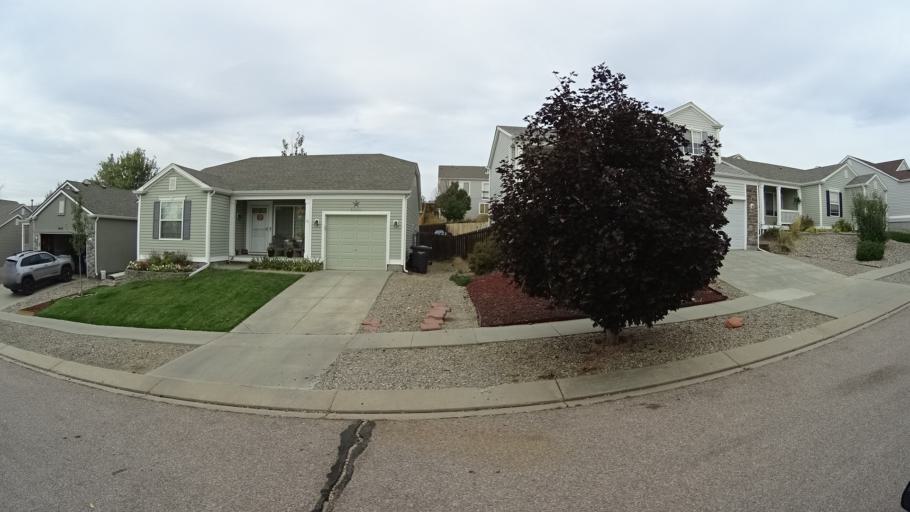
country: US
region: Colorado
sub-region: El Paso County
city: Cimarron Hills
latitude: 38.9245
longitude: -104.7038
